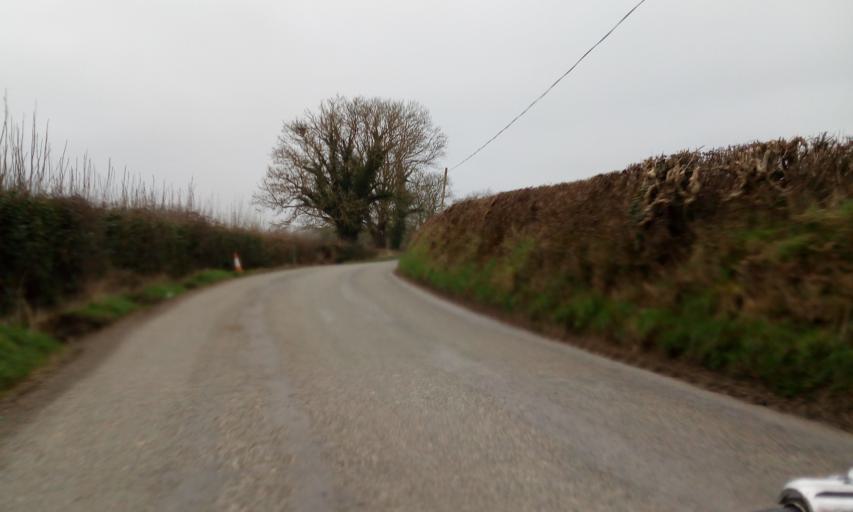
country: IE
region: Leinster
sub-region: Kilkenny
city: Kilkenny
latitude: 52.6580
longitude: -7.1848
